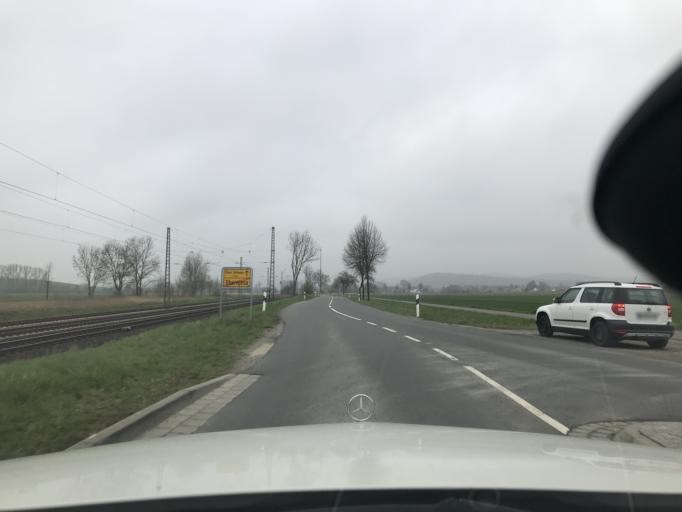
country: DE
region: Lower Saxony
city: Gemeinde Friedland
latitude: 51.4558
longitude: 9.9192
